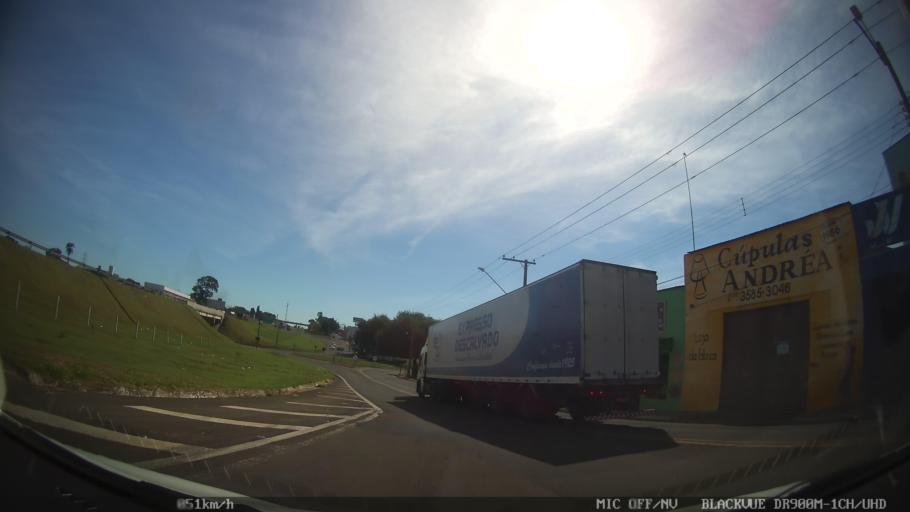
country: BR
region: Sao Paulo
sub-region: Porto Ferreira
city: Porto Ferreira
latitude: -21.8670
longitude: -47.4900
